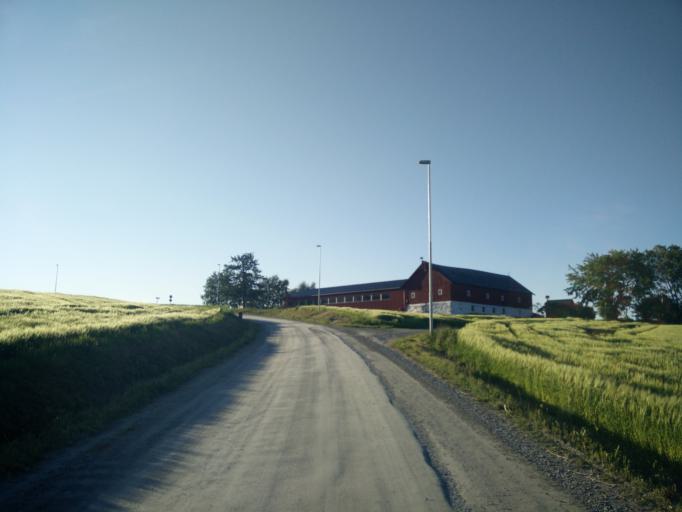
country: NO
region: Sor-Trondelag
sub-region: Skaun
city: Borsa
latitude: 63.3305
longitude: 10.0644
